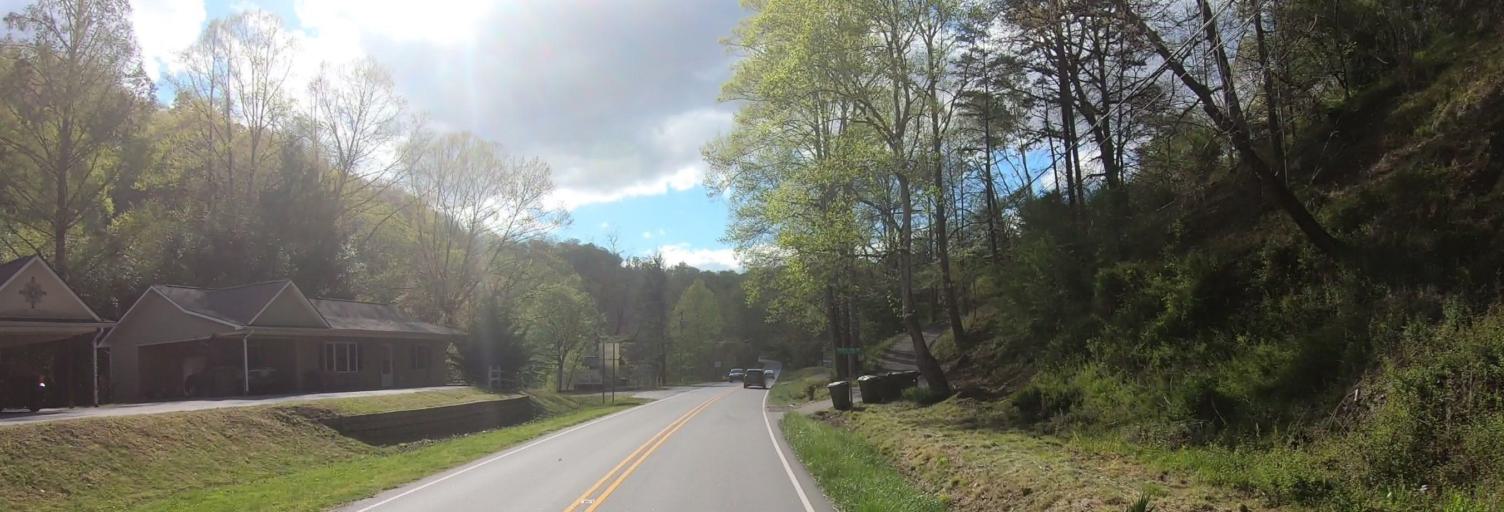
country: US
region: North Carolina
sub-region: Swain County
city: Cherokee
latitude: 35.4577
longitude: -83.3636
